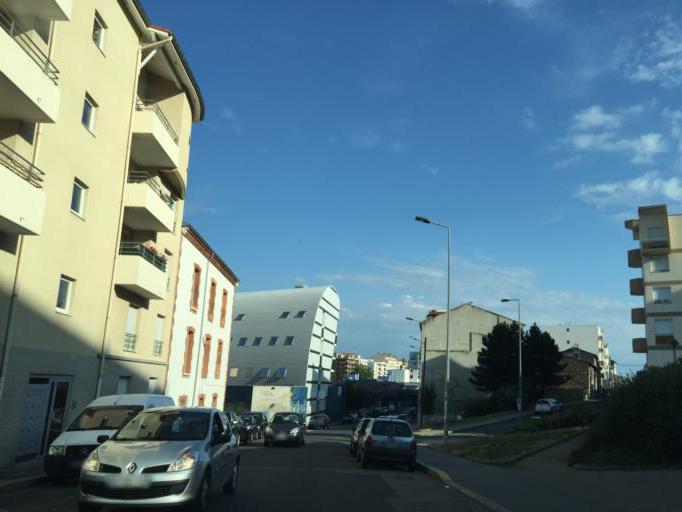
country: FR
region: Rhone-Alpes
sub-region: Departement de la Loire
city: Saint-Etienne
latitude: 45.4257
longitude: 4.3946
